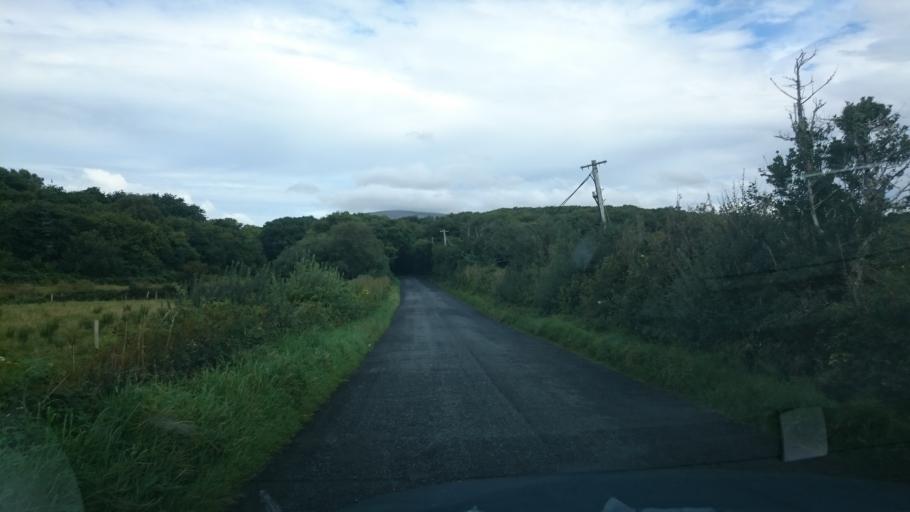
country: IE
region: Connaught
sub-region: Maigh Eo
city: Westport
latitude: 53.9013
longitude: -9.5501
